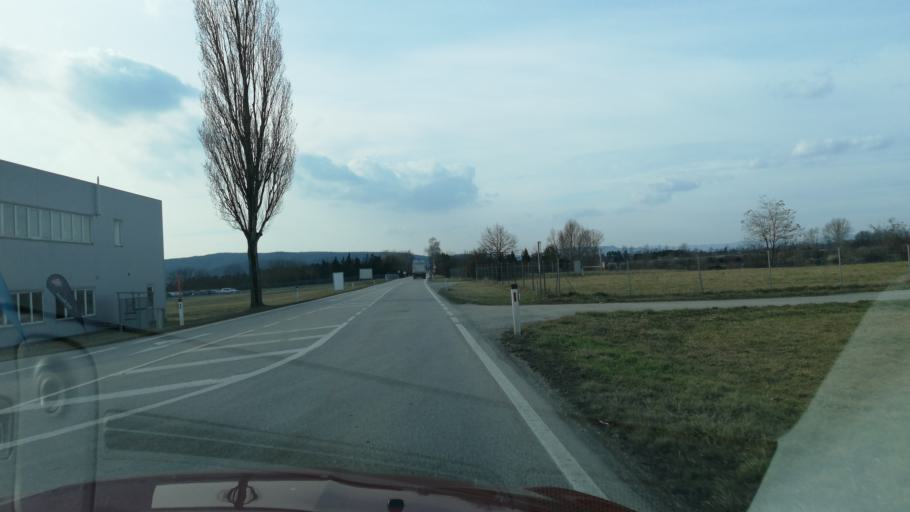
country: AT
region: Lower Austria
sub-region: Politischer Bezirk Tulln
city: Grafenworth
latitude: 48.3356
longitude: 15.8245
